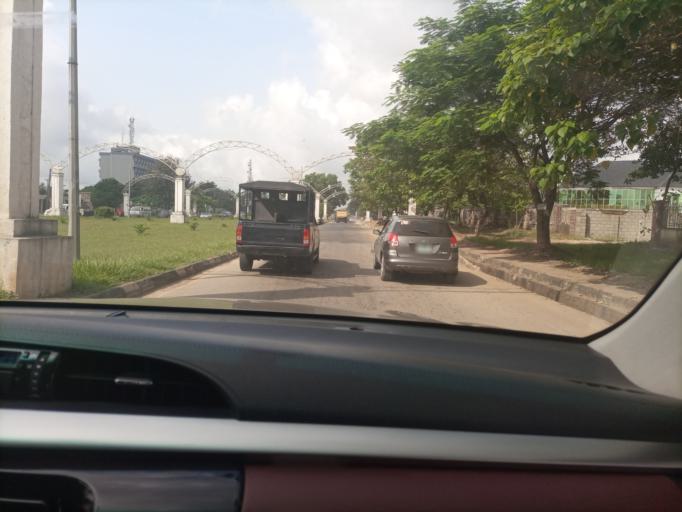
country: NG
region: Imo
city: Owerri
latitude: 5.4748
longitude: 7.0219
